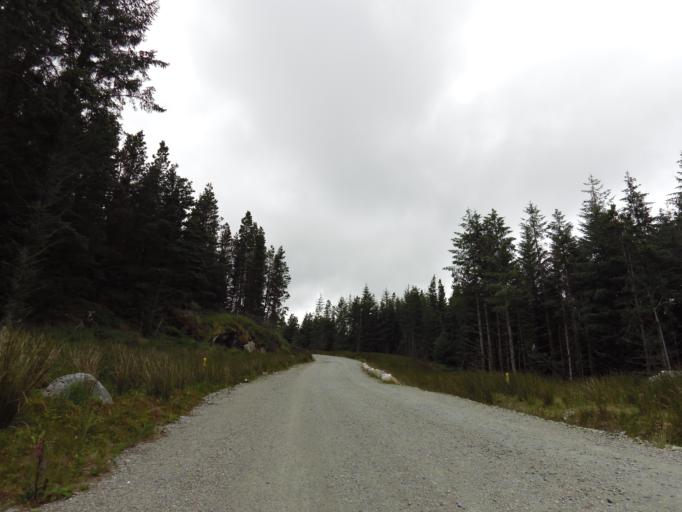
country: IE
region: Connaught
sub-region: County Galway
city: Oughterard
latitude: 53.3811
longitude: -9.3682
